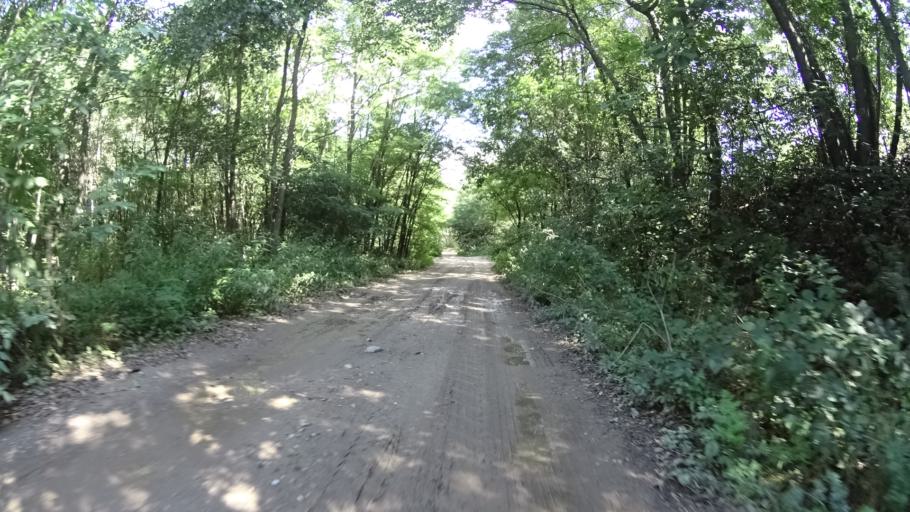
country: PL
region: Masovian Voivodeship
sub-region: Powiat grojecki
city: Mogielnica
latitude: 51.6719
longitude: 20.7465
